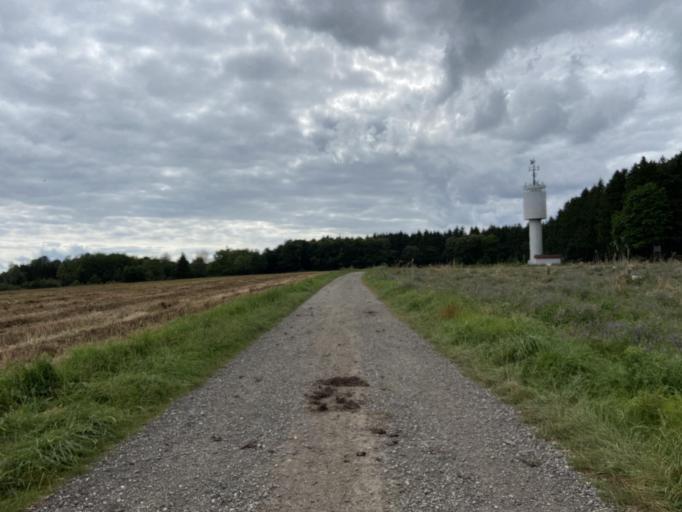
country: DE
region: Baden-Wuerttemberg
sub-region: Tuebingen Region
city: Sigmaringendorf
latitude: 48.0796
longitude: 9.2540
